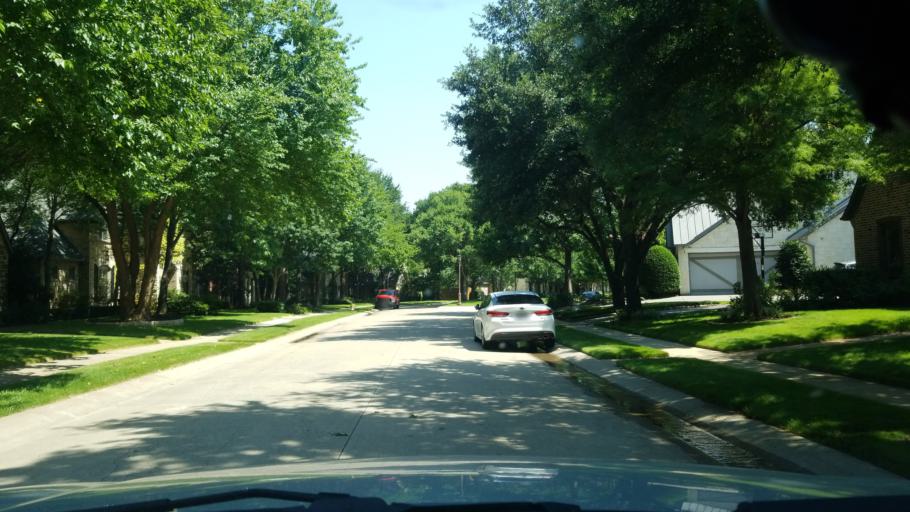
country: US
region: Texas
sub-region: Dallas County
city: Coppell
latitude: 32.9513
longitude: -96.9969
